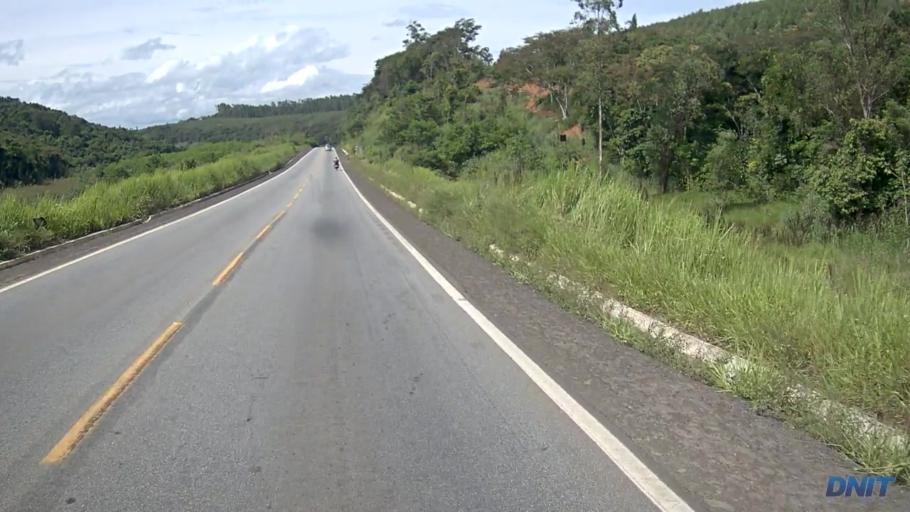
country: BR
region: Minas Gerais
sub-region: Ipaba
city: Ipaba
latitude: -19.4110
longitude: -42.4890
